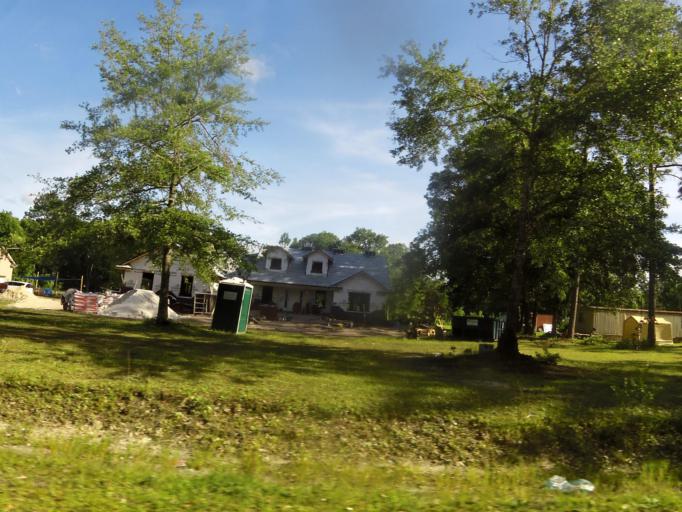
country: US
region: Florida
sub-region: Nassau County
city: Nassau Village-Ratliff
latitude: 30.5190
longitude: -81.7721
